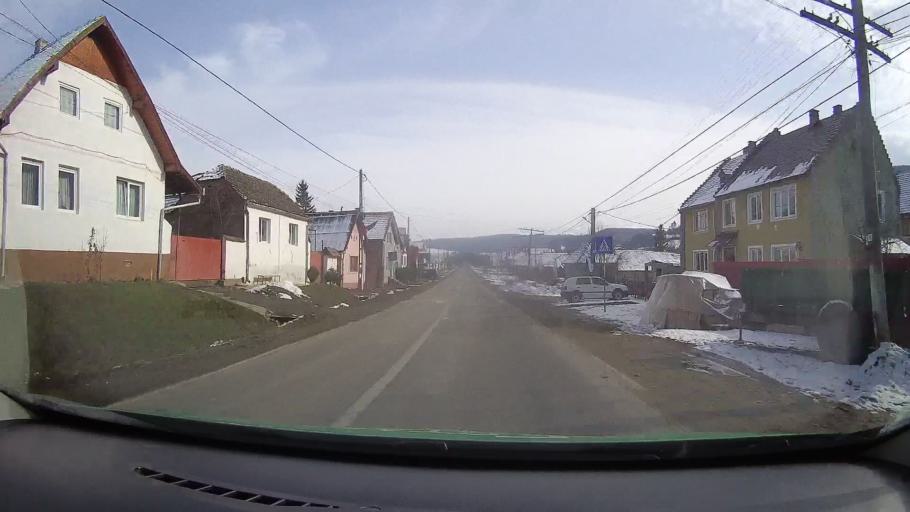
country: RO
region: Mures
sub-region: Comuna Apold
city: Saes
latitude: 46.1499
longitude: 24.7718
